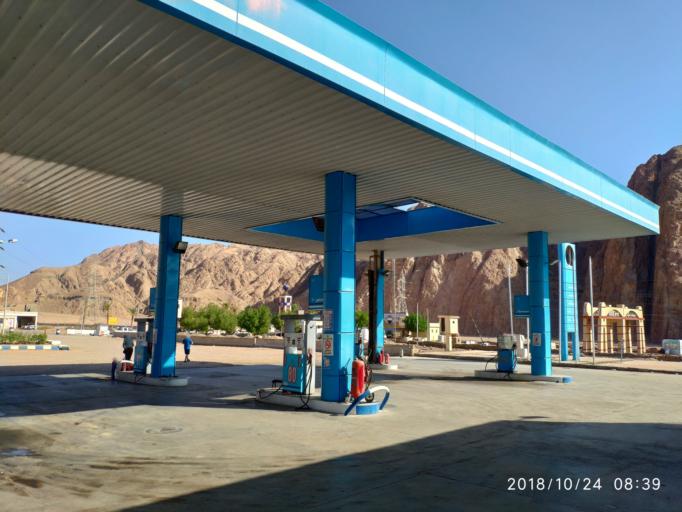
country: EG
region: South Sinai
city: Dhahab
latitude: 28.5220
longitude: 34.4716
